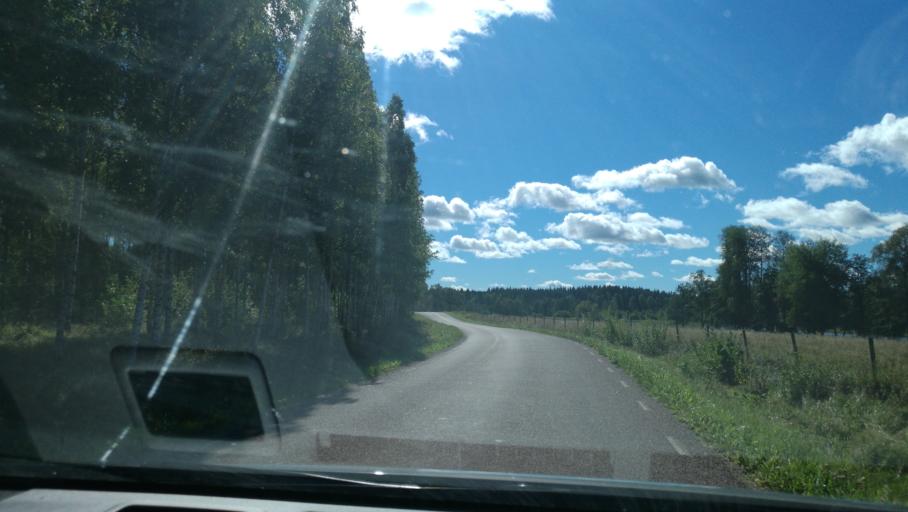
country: SE
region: Vaestmanland
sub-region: Hallstahammars Kommun
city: Hallstahammar
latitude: 59.6565
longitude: 16.1948
